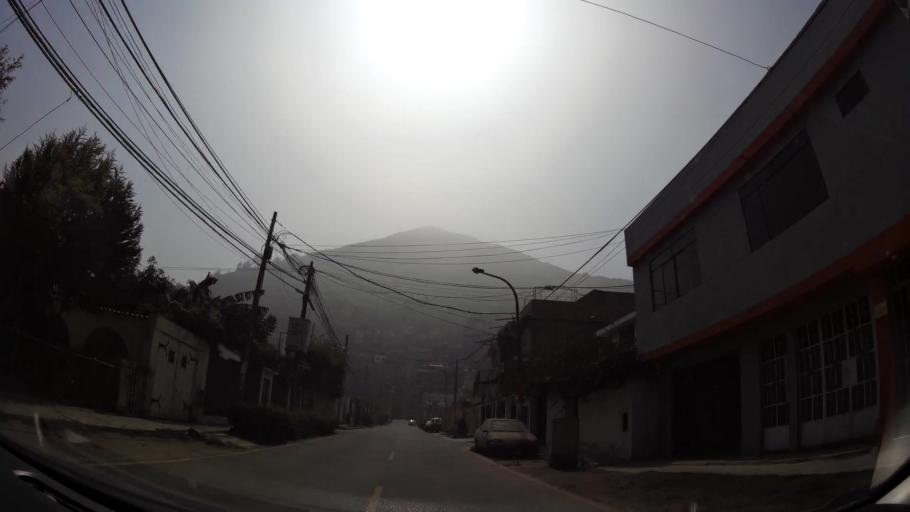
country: PE
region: Lima
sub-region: Lima
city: Chosica
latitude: -11.9426
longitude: -76.7066
